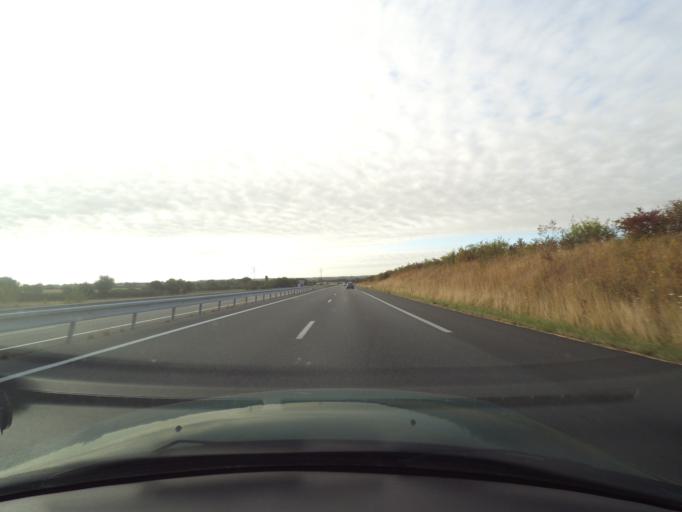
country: FR
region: Pays de la Loire
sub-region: Departement de Maine-et-Loire
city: La Tessoualle
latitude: 46.9773
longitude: -0.8164
